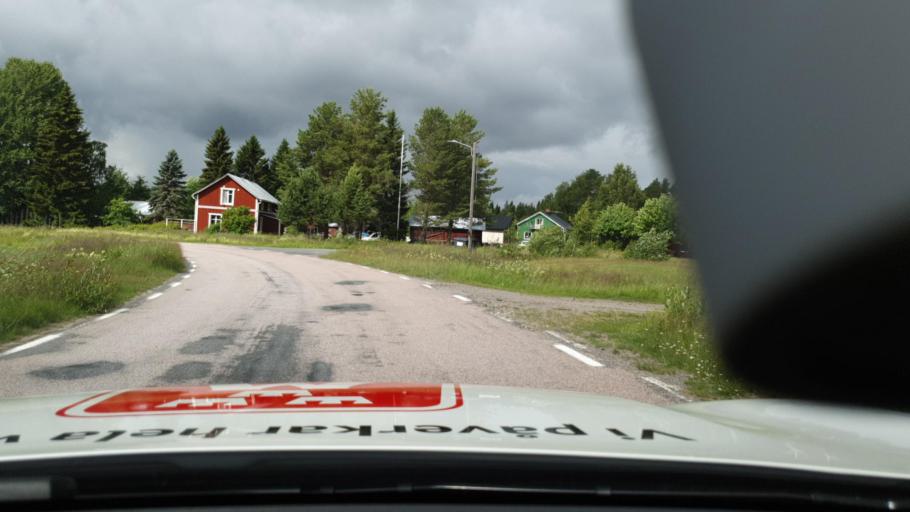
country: SE
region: Norrbotten
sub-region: Lulea Kommun
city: Sodra Sunderbyn
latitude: 65.4909
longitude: 21.9246
